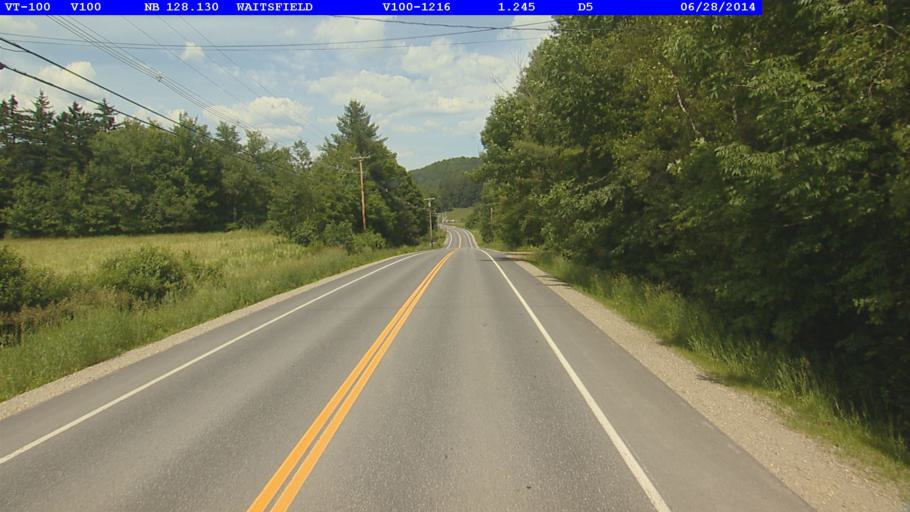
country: US
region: Vermont
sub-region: Washington County
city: Northfield
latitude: 44.1636
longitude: -72.8332
